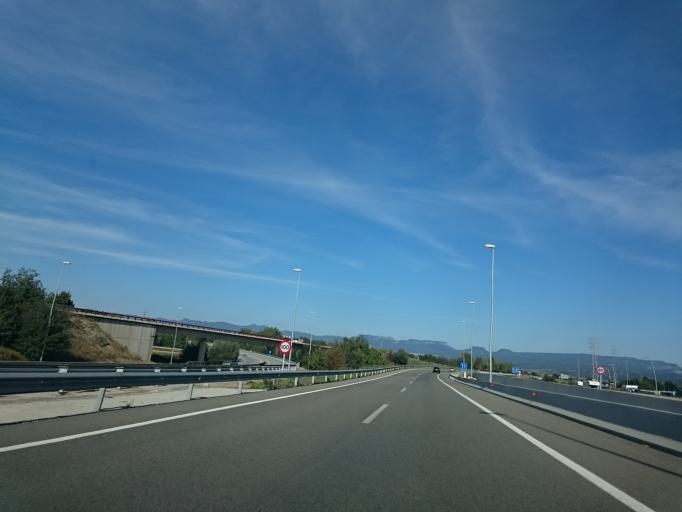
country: ES
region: Catalonia
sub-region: Provincia de Barcelona
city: Gurb
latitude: 41.9566
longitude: 2.2453
